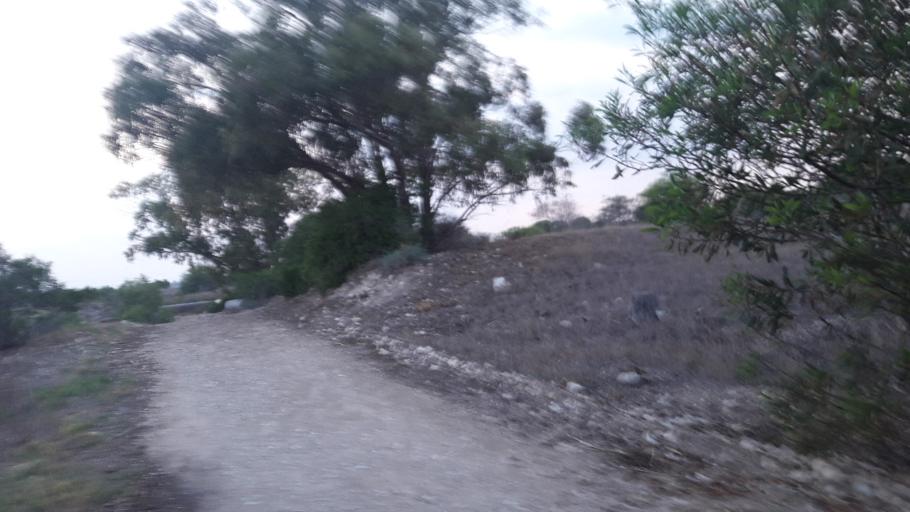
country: CY
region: Ammochostos
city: Famagusta
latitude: 35.1810
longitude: 33.9008
